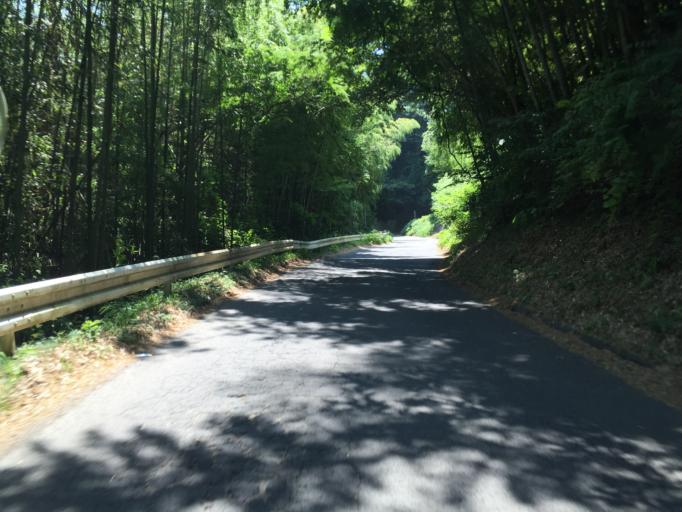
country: JP
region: Fukushima
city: Yanagawamachi-saiwaicho
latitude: 37.9043
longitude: 140.6602
